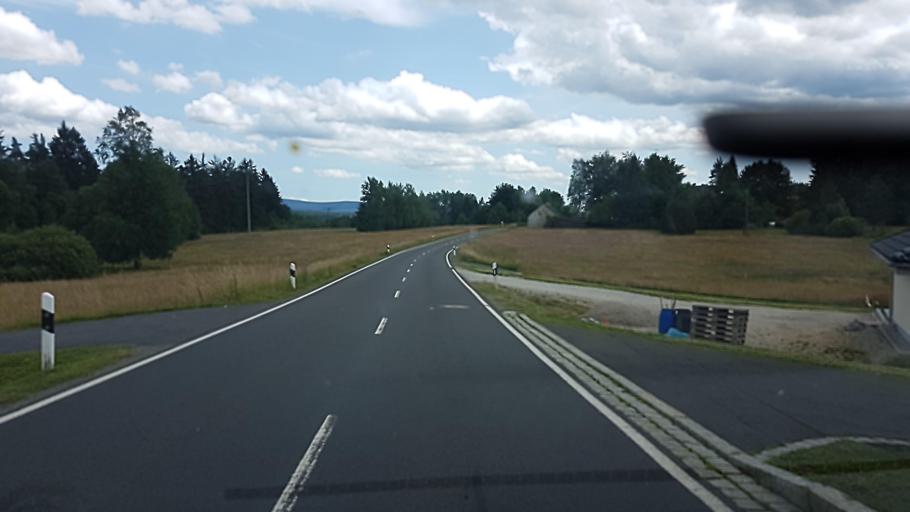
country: DE
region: Bavaria
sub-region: Upper Franconia
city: Nagel
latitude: 49.9875
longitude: 11.9041
